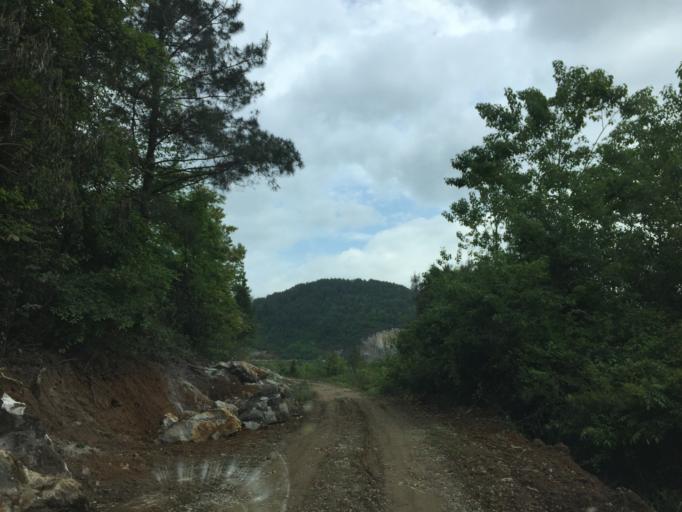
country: CN
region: Guizhou Sheng
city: Kuanping
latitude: 28.0149
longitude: 108.0723
